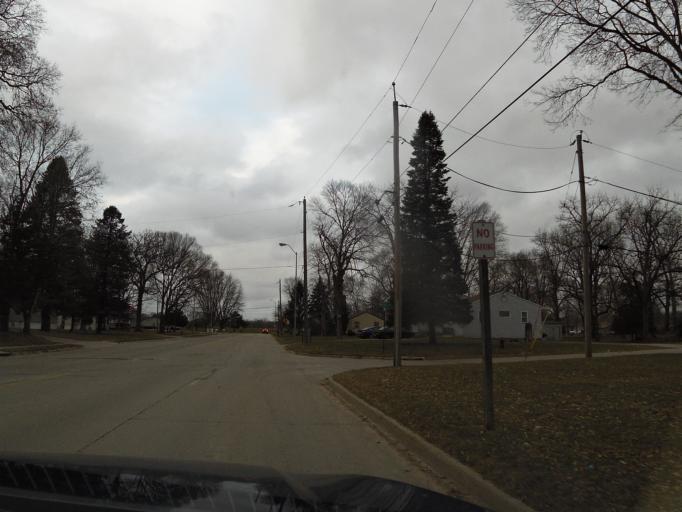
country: US
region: Iowa
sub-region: Black Hawk County
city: Evansdale
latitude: 42.4674
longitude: -92.2975
